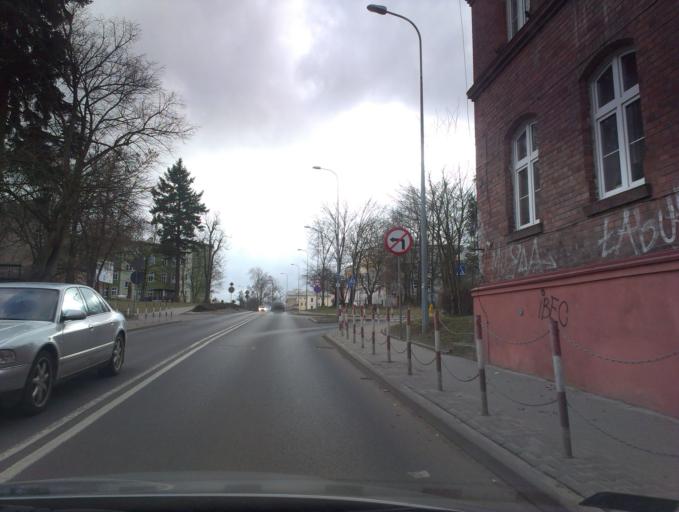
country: PL
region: West Pomeranian Voivodeship
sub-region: Koszalin
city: Koszalin
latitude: 54.1925
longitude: 16.1939
